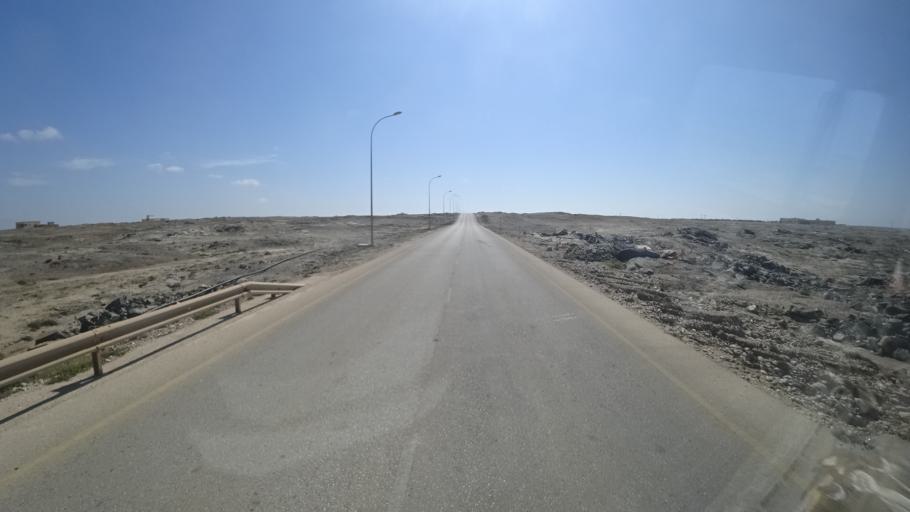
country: OM
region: Zufar
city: Salalah
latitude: 16.9684
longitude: 54.7305
